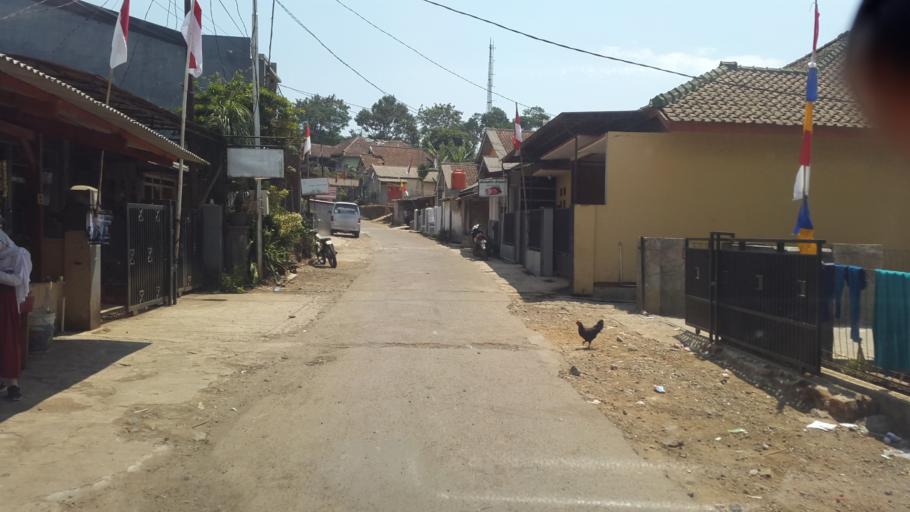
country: ID
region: West Java
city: Cigaru
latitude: -7.1001
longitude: 106.5950
